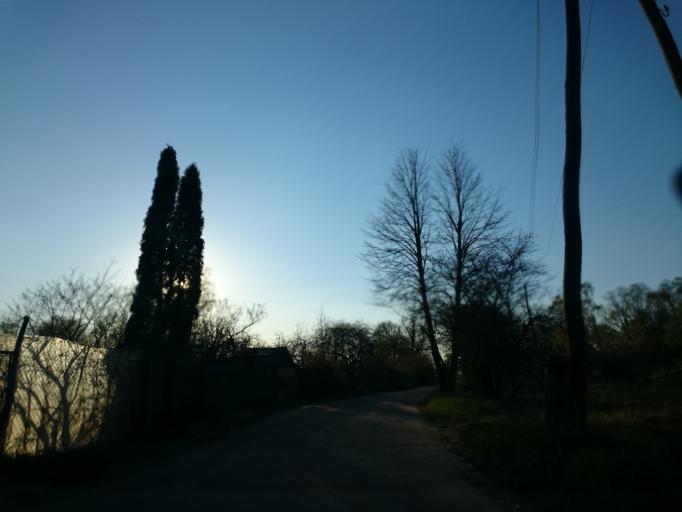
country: LV
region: Adazi
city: Adazi
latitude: 57.0819
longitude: 24.3280
